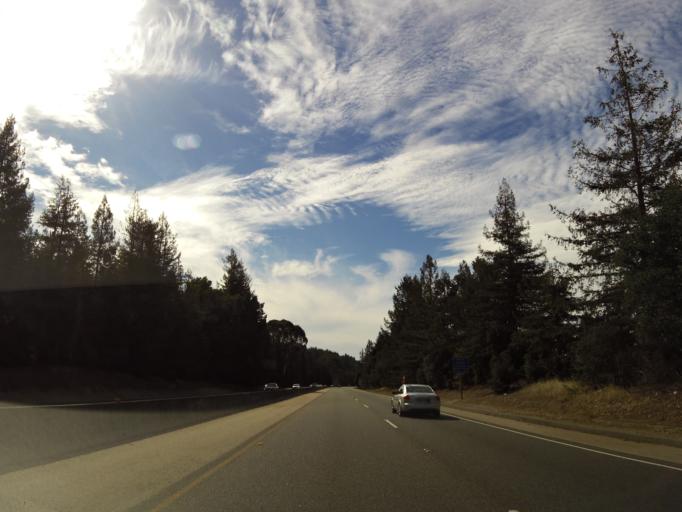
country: US
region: California
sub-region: Santa Cruz County
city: Scotts Valley
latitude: 37.0562
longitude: -122.0072
